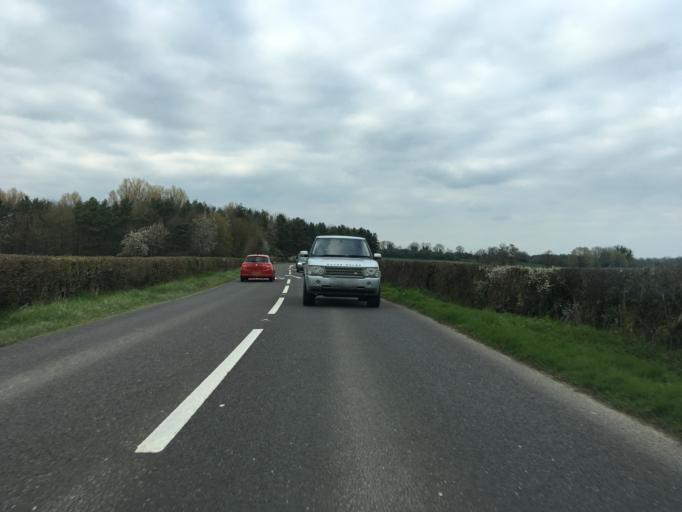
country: GB
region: England
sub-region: Gloucestershire
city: Coates
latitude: 51.6812
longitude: -2.0141
